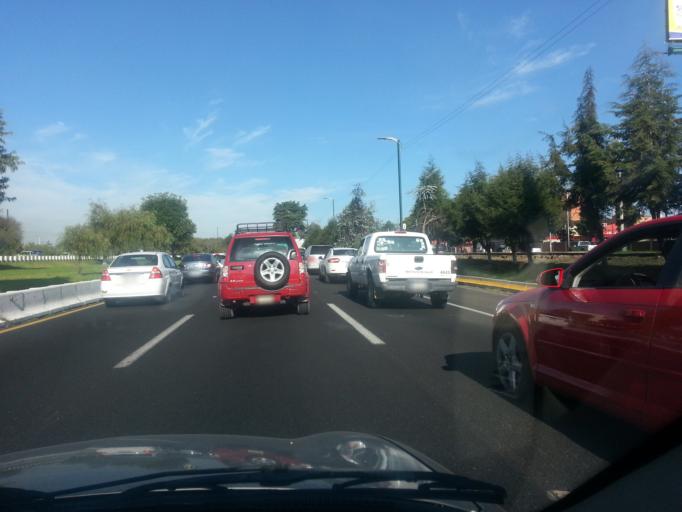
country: MX
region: Mexico
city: Santa Maria Totoltepec
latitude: 19.2880
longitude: -99.6148
